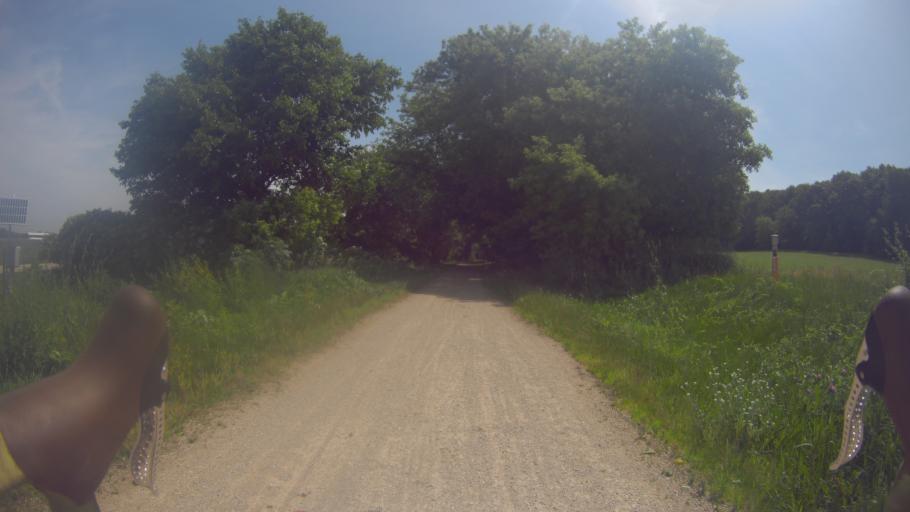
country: US
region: Wisconsin
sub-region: Jefferson County
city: Lake Mills
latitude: 43.0651
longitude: -88.9575
